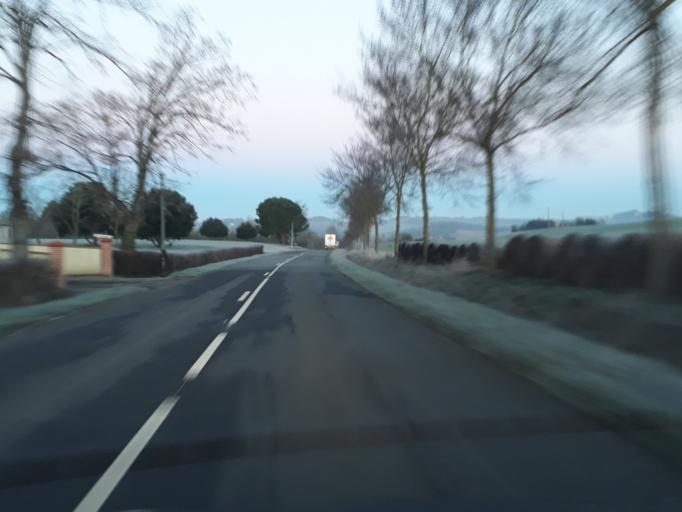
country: FR
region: Midi-Pyrenees
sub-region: Departement du Gers
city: Samatan
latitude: 43.5020
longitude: 0.9058
